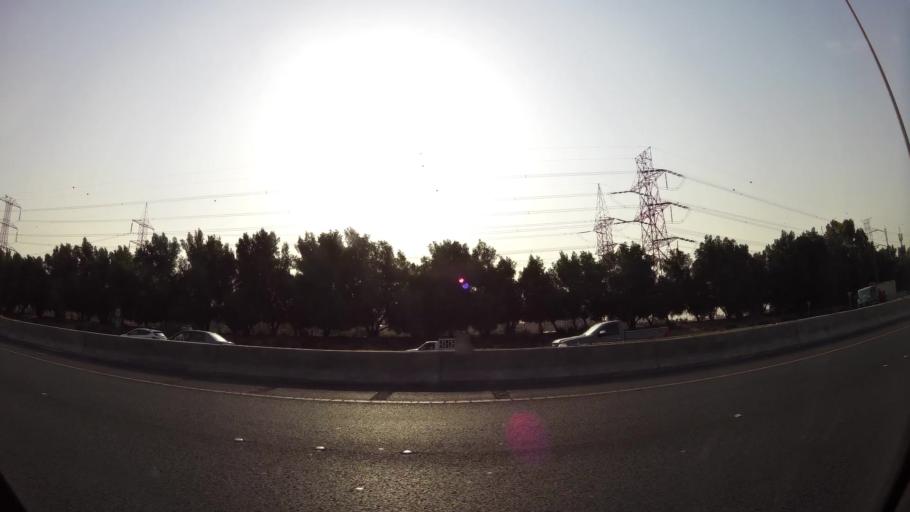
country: KW
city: Bayan
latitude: 29.2772
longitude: 48.0364
